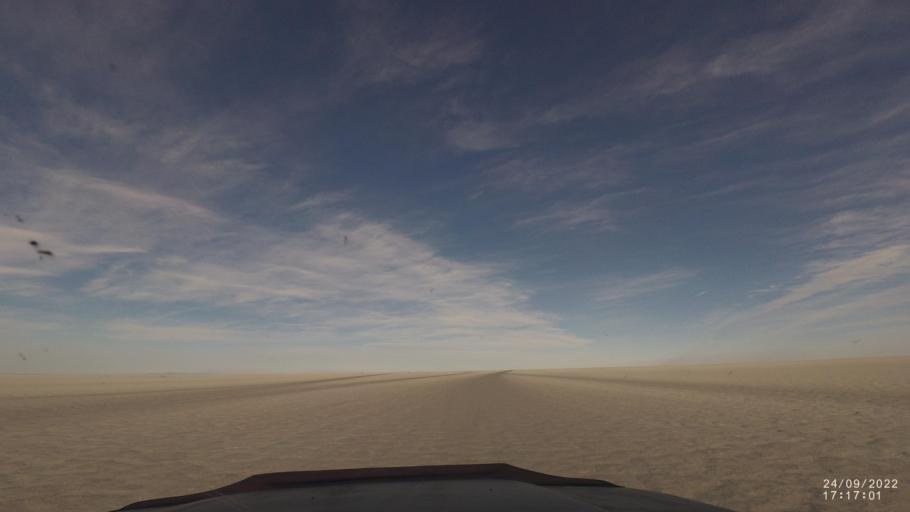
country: BO
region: Potosi
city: Colchani
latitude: -20.2390
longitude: -67.6211
